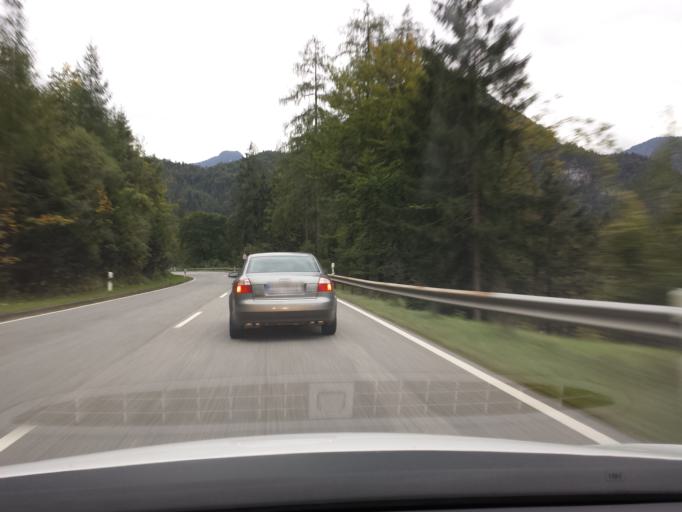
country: DE
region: Bavaria
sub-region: Upper Bavaria
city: Schneizlreuth
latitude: 47.6800
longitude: 12.8324
